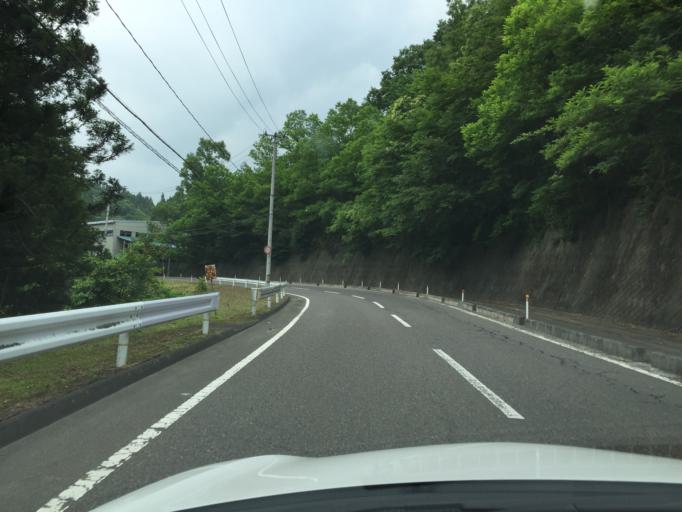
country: JP
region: Fukushima
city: Funehikimachi-funehiki
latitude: 37.2892
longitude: 140.5904
